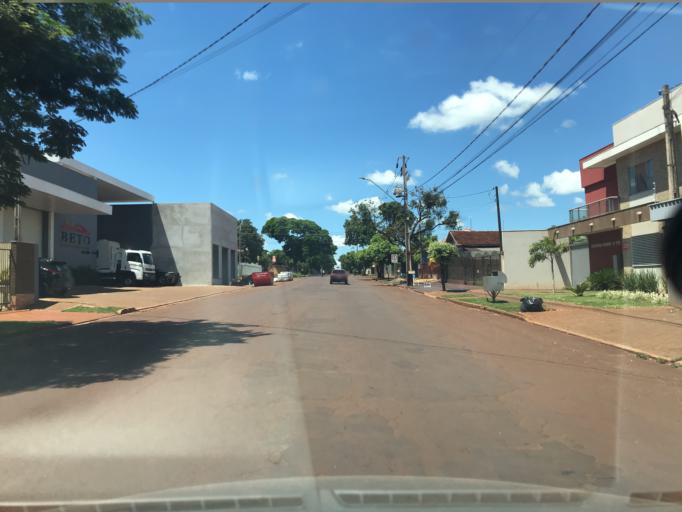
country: BR
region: Parana
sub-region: Palotina
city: Palotina
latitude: -24.2874
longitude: -53.8462
